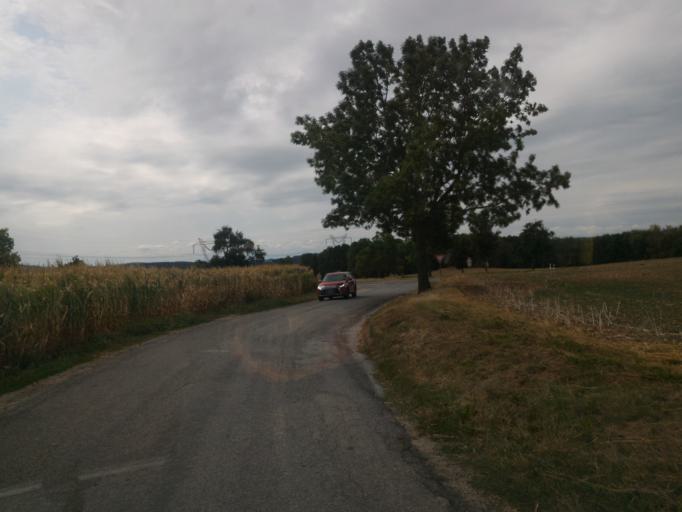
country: CZ
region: Jihocesky
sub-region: Okres Jindrichuv Hradec
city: Dacice
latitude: 49.1002
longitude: 15.4147
